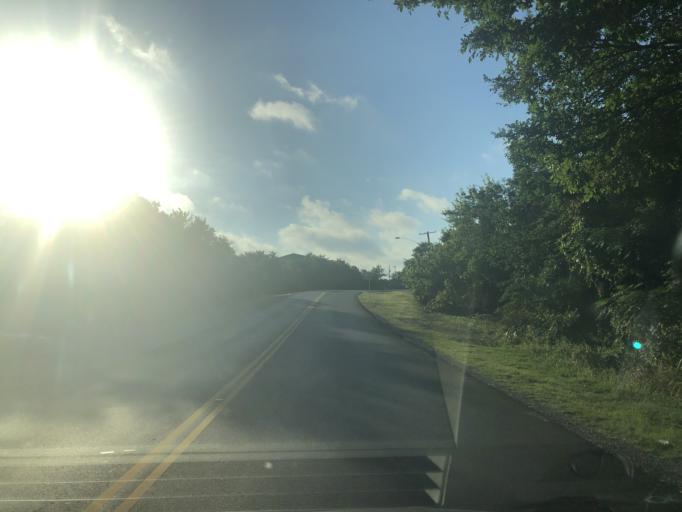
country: US
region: Texas
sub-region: Dallas County
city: Duncanville
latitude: 32.6651
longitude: -96.9500
